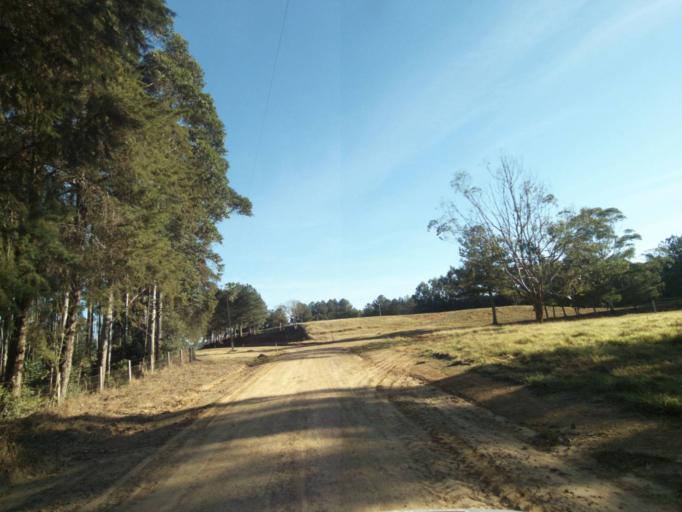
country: BR
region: Parana
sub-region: Telemaco Borba
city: Telemaco Borba
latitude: -24.5132
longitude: -50.6608
